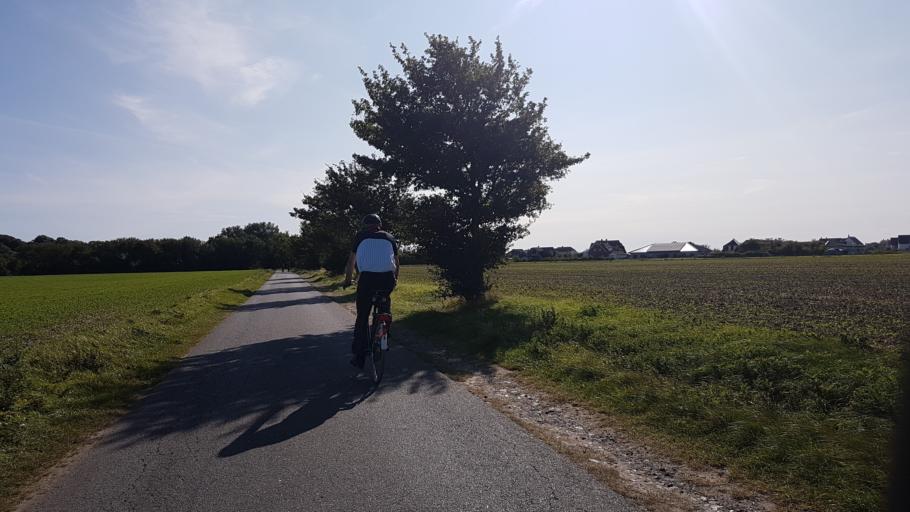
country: DE
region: Mecklenburg-Vorpommern
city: Dranske
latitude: 54.6552
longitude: 13.2573
